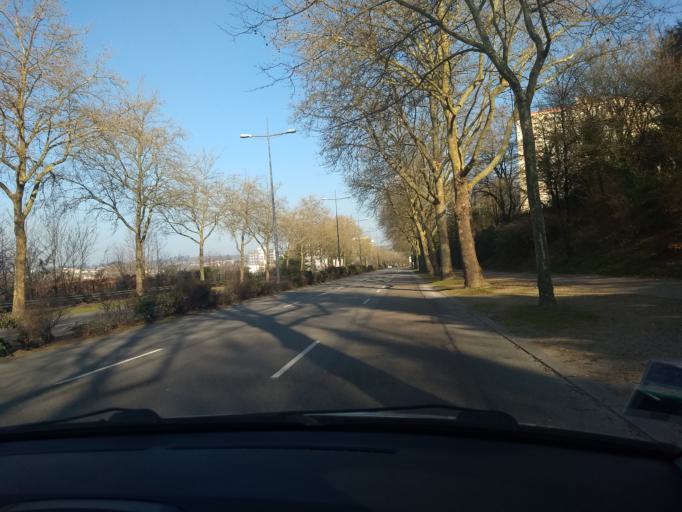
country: FR
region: Limousin
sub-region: Departement de la Haute-Vienne
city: Isle
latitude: 45.8290
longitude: 1.2267
